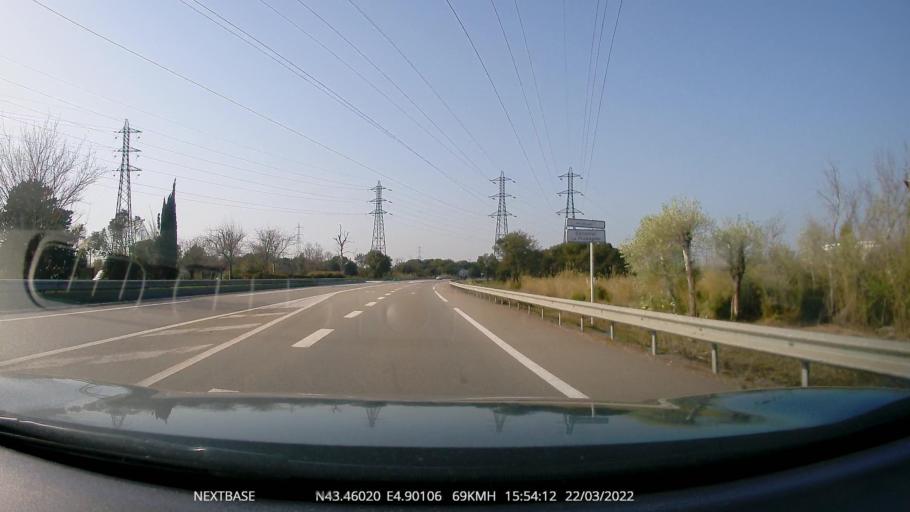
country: FR
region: Provence-Alpes-Cote d'Azur
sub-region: Departement des Bouches-du-Rhone
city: Fos-sur-Mer
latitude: 43.4603
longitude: 4.9010
